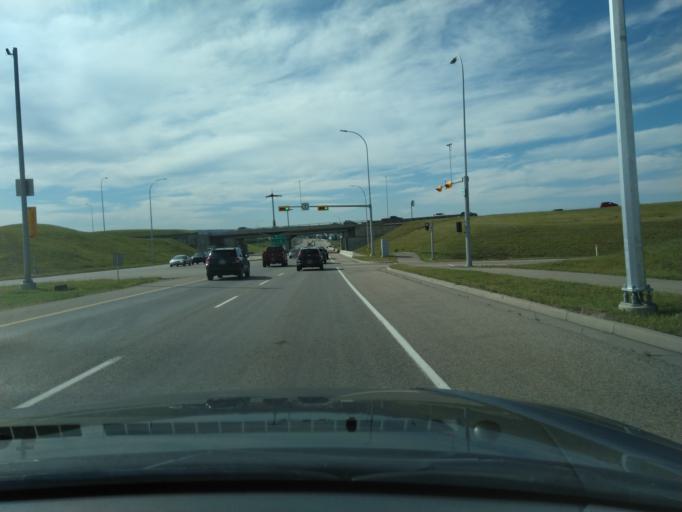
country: CA
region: Alberta
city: Calgary
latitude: 51.1409
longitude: -114.0326
